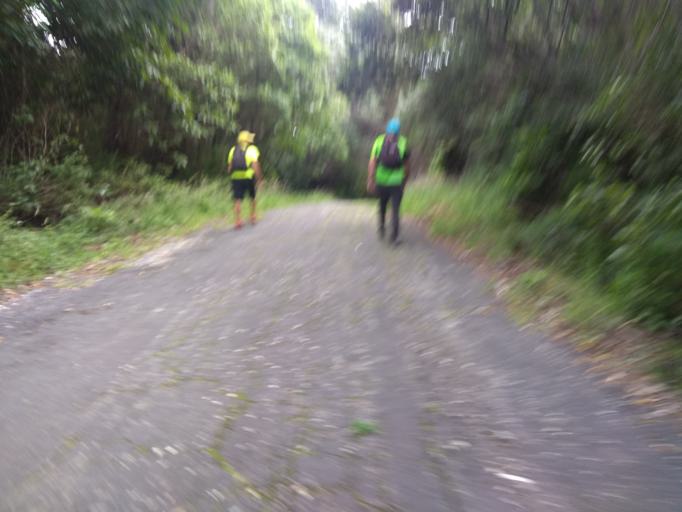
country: CR
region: Cartago
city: Cot
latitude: 9.9650
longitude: -83.8753
